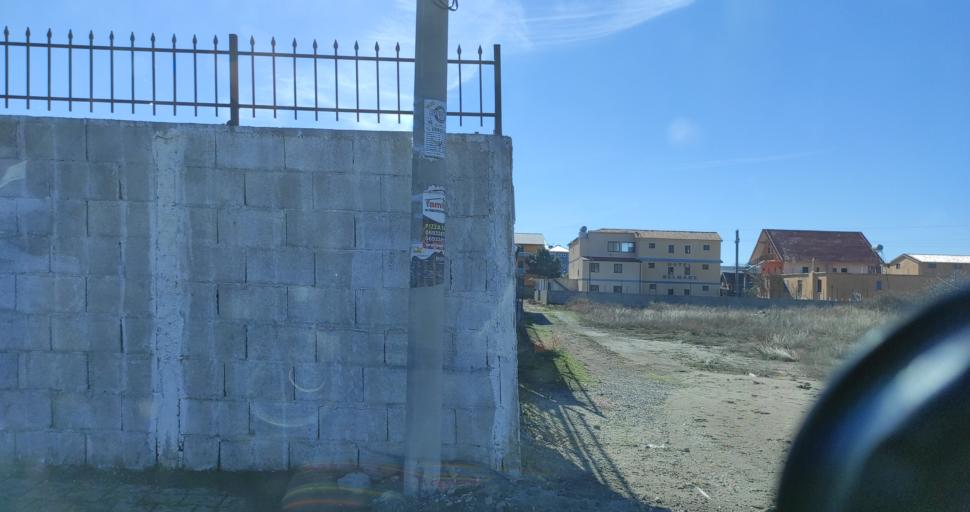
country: AL
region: Shkoder
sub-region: Rrethi i Shkodres
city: Velipoje
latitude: 41.8653
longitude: 19.4386
